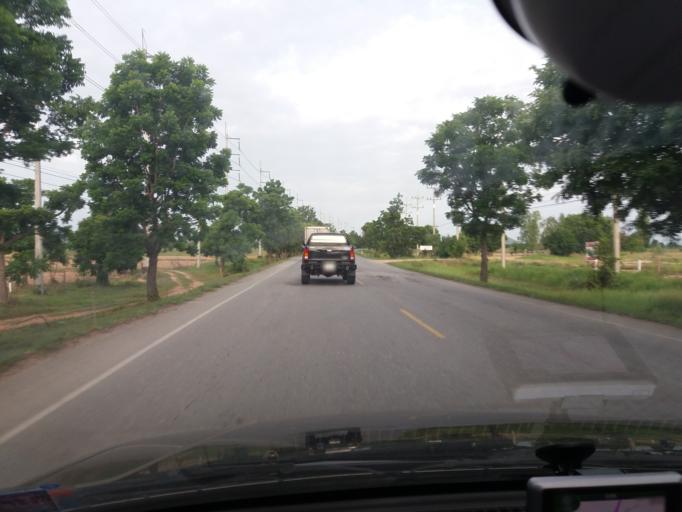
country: TH
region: Kanchanaburi
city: Huai Krachao
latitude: 14.3331
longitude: 99.7469
